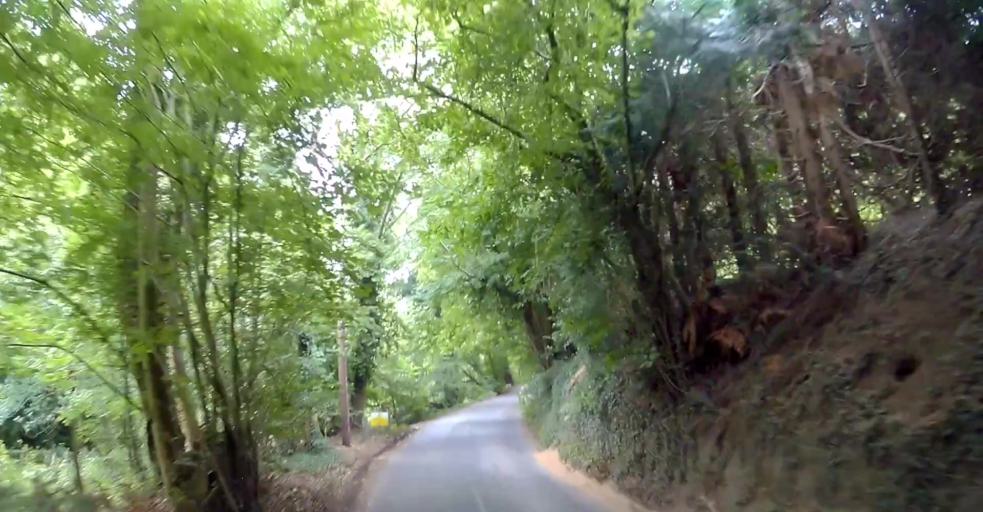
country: GB
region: England
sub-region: Surrey
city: Hale
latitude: 51.2126
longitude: -0.7728
